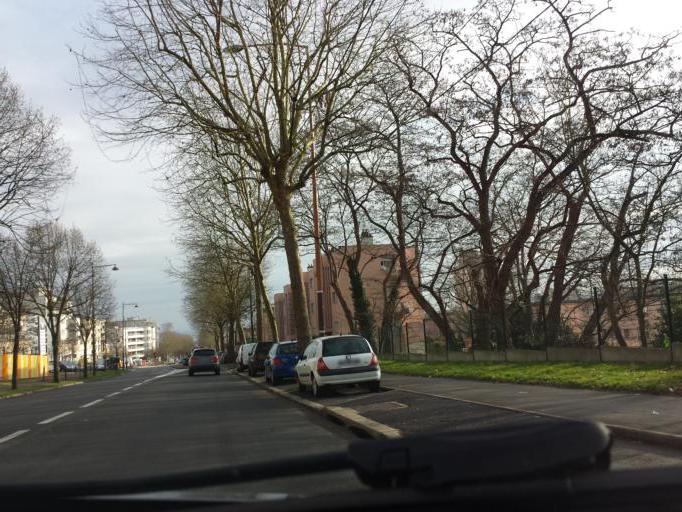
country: FR
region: Ile-de-France
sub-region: Departement des Hauts-de-Seine
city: Chatenay-Malabry
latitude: 48.7658
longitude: 2.2577
